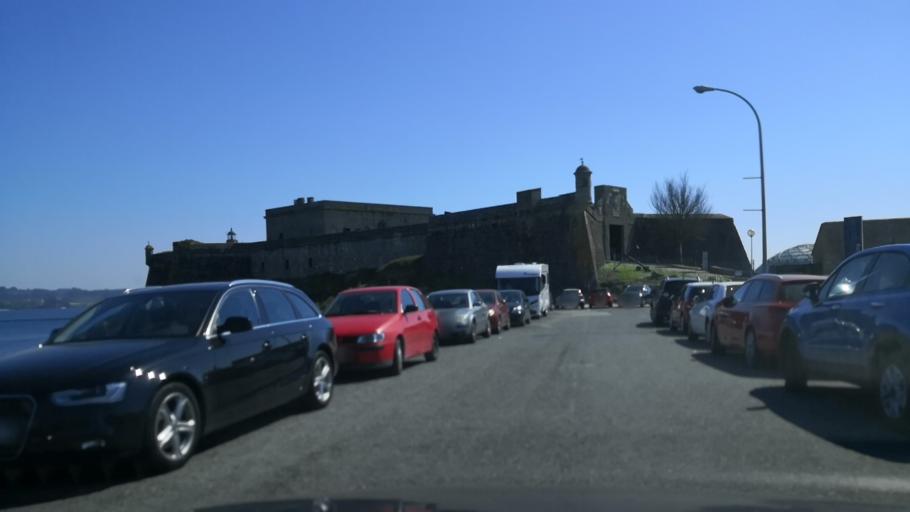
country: ES
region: Galicia
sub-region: Provincia da Coruna
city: A Coruna
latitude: 43.3665
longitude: -8.3888
